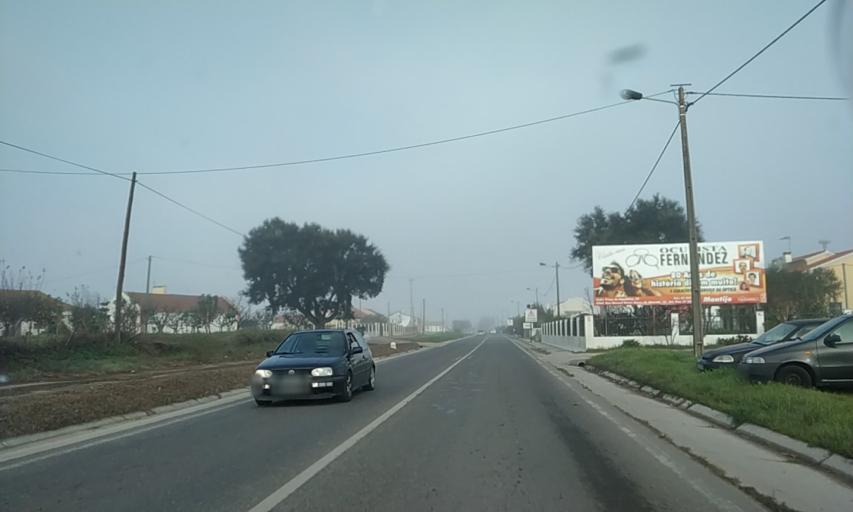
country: PT
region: Setubal
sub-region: Palmela
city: Pinhal Novo
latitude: 38.6621
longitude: -8.9238
